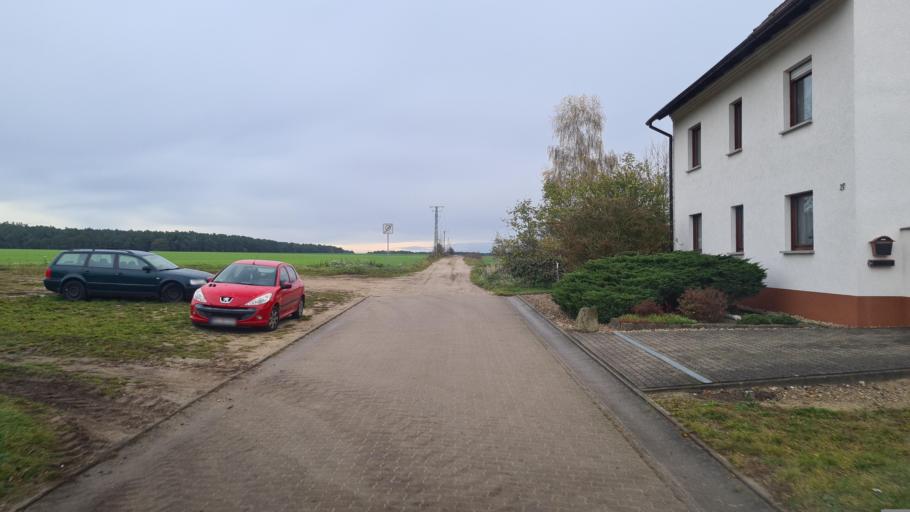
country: DE
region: Saxony-Anhalt
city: Abtsdorf
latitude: 51.9320
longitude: 12.6835
